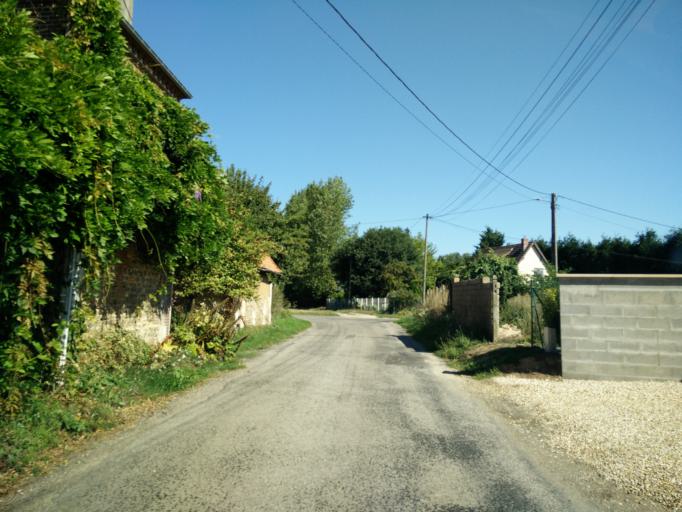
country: FR
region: Haute-Normandie
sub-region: Departement de l'Eure
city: La Haye-Malherbe
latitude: 49.1704
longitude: 1.0062
